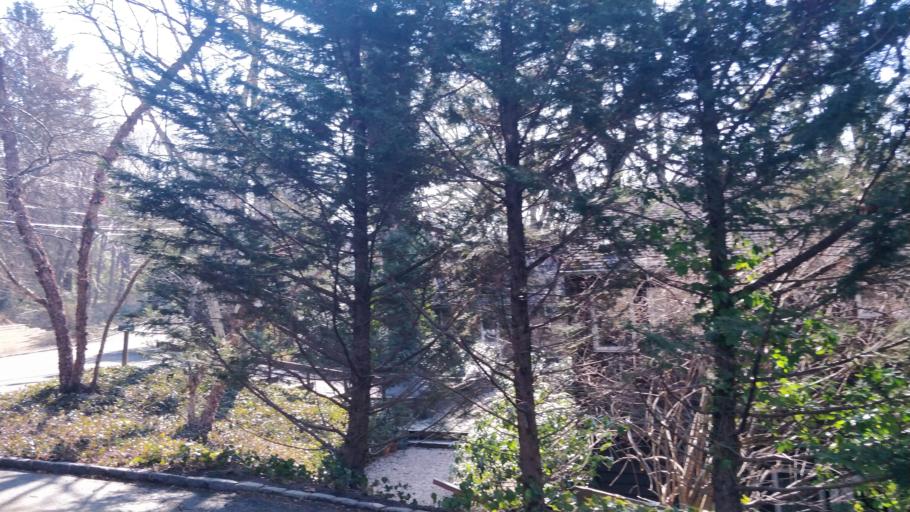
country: US
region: New York
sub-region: Nassau County
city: Sea Cliff
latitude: 40.8408
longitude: -73.6458
